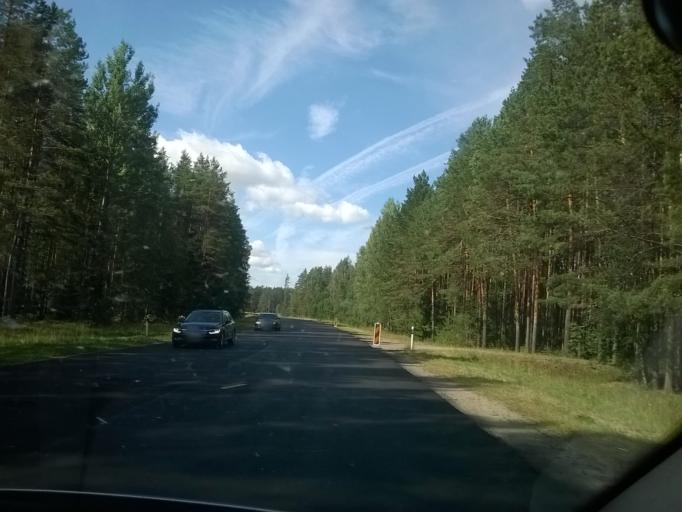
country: EE
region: Vorumaa
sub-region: Voru linn
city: Voru
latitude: 57.8123
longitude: 26.9769
